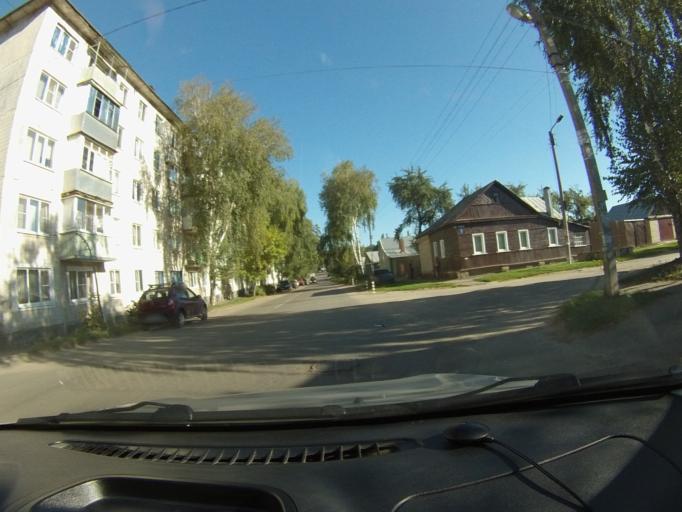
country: RU
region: Tambov
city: Tambov
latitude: 52.7563
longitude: 41.4247
